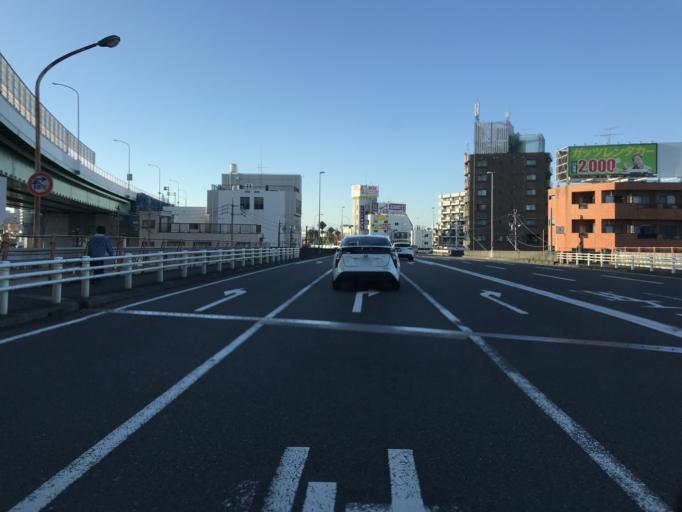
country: JP
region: Aichi
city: Nagoya-shi
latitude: 35.1565
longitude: 136.8717
